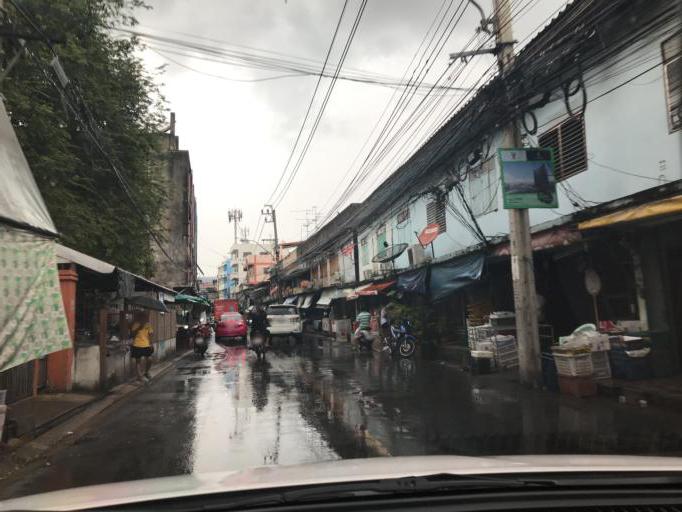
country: TH
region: Bangkok
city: Phasi Charoen
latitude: 13.7171
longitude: 100.4441
